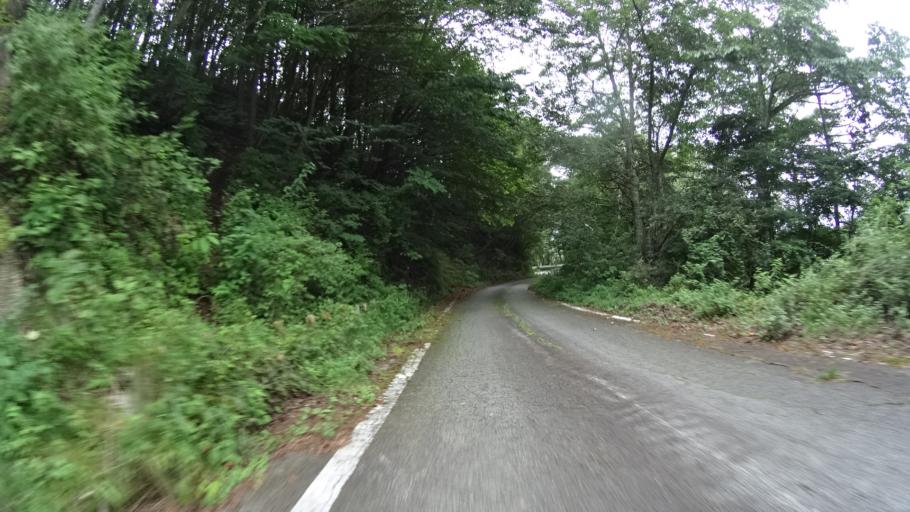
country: JP
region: Yamanashi
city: Nirasaki
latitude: 35.8104
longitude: 138.5473
